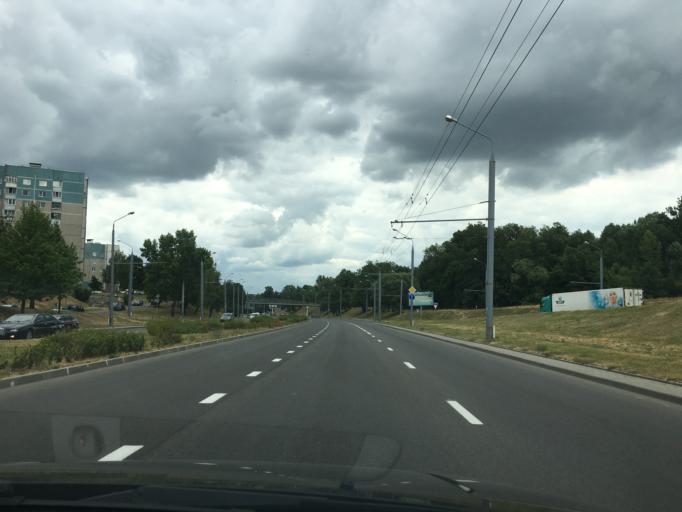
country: BY
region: Grodnenskaya
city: Hrodna
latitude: 53.6534
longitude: 23.8553
